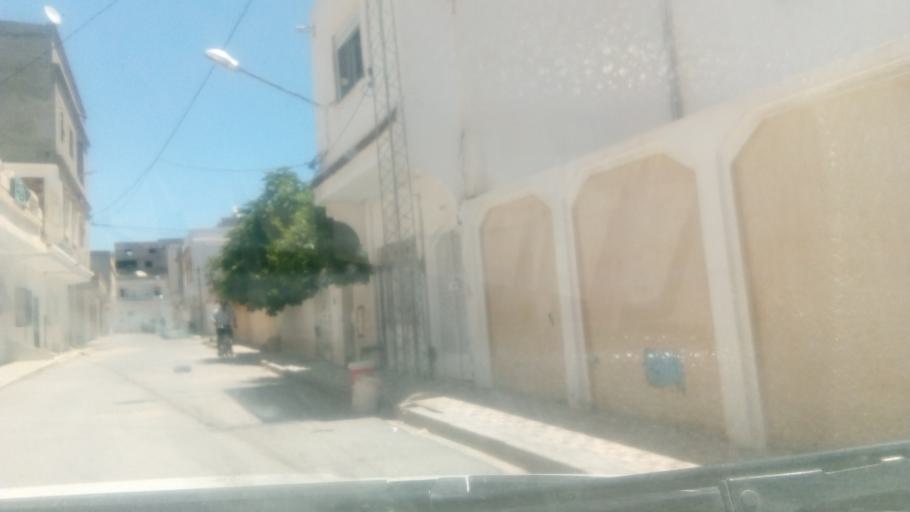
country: TN
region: Al Qayrawan
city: Kairouan
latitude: 35.6677
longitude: 10.0873
